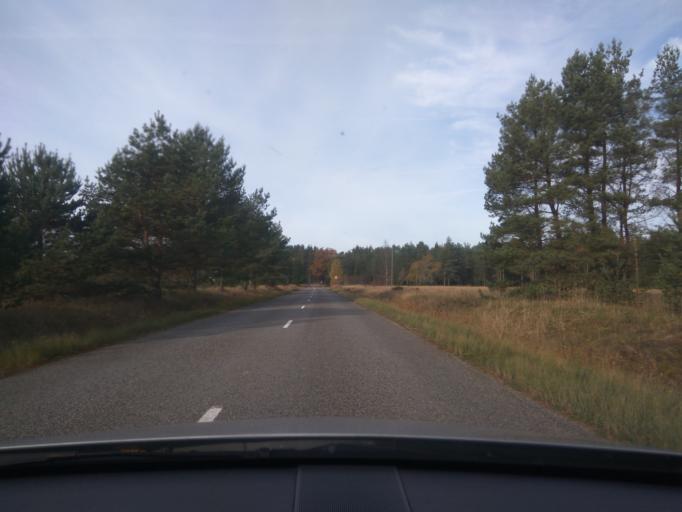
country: LV
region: Alsunga
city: Alsunga
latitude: 56.9892
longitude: 21.5033
